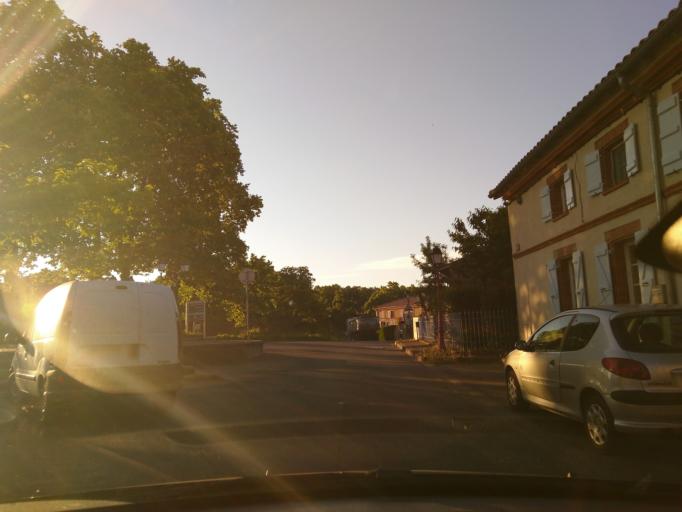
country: FR
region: Midi-Pyrenees
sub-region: Departement de la Haute-Garonne
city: Merville
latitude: 43.7189
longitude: 1.2992
